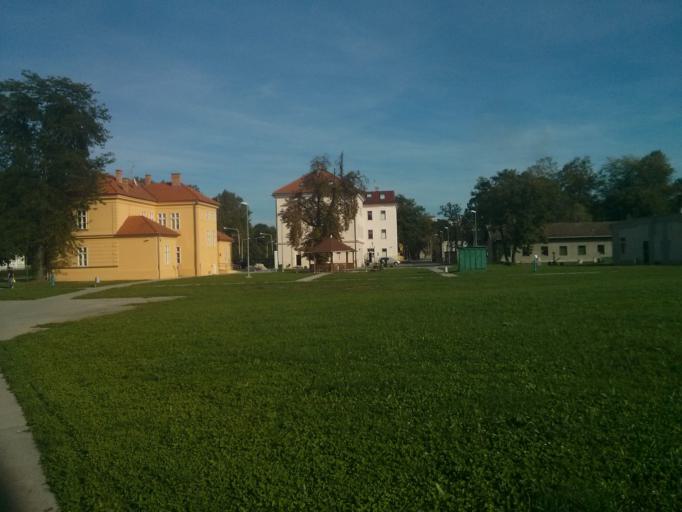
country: HR
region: Osjecko-Baranjska
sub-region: Grad Osijek
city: Osijek
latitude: 45.5570
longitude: 18.7102
